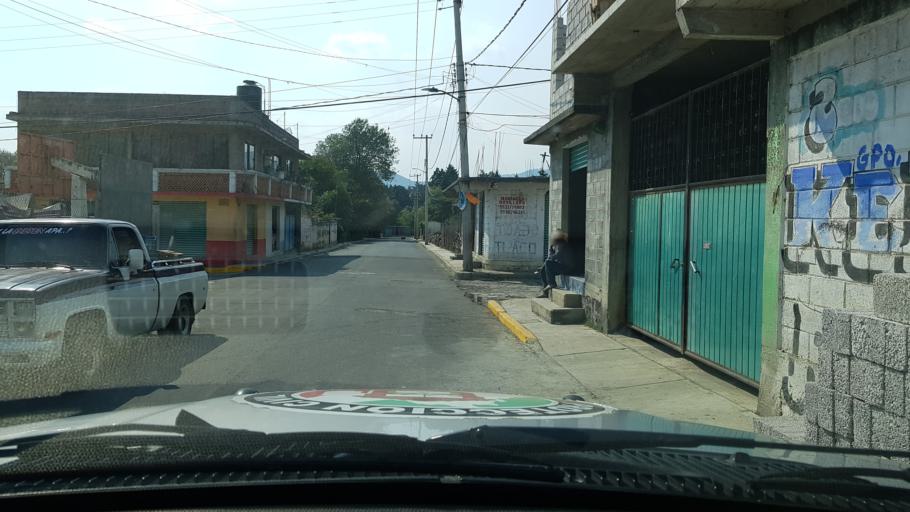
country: MX
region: Mexico
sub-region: Ozumba
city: San Jose Tlacotitlan
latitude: 18.9841
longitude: -98.8096
